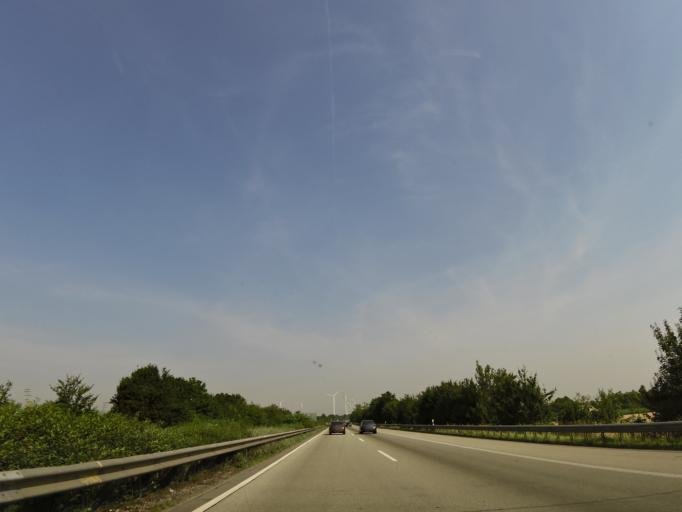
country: DE
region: Rheinland-Pfalz
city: Grossniedesheim
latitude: 49.5640
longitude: 8.3062
